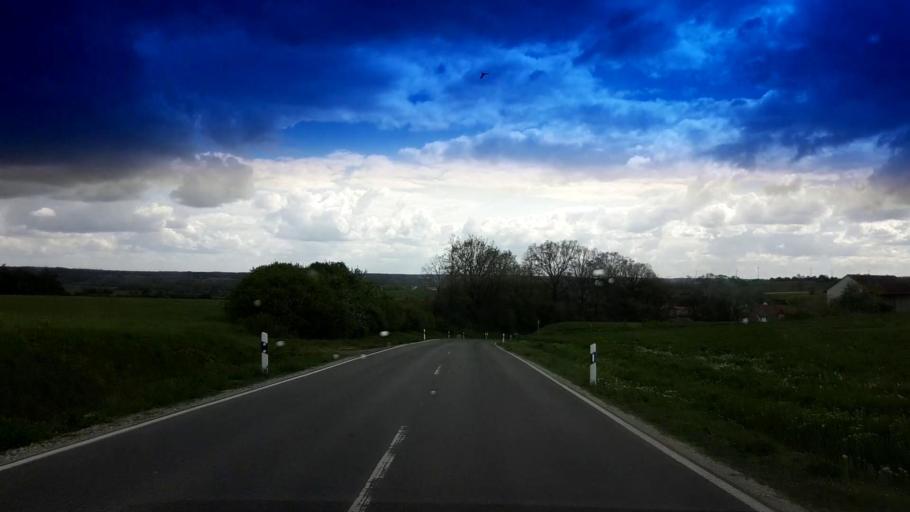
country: DE
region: Bavaria
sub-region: Upper Franconia
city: Pommersfelden
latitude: 49.7880
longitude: 10.8250
